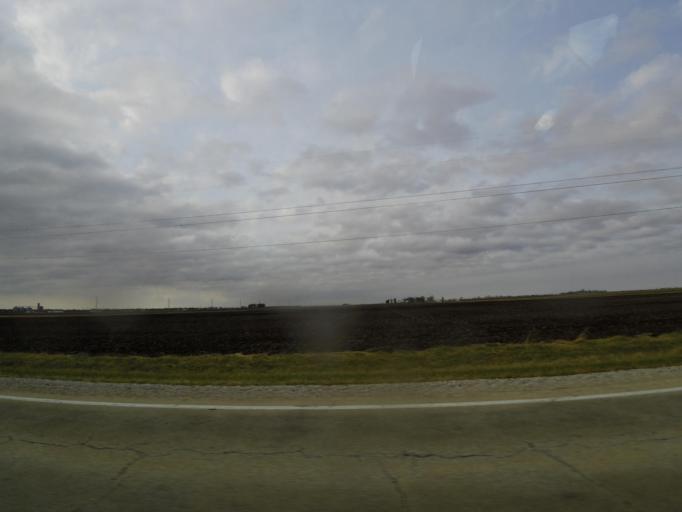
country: US
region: Illinois
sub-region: Christian County
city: Pana
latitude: 39.4171
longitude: -89.0439
